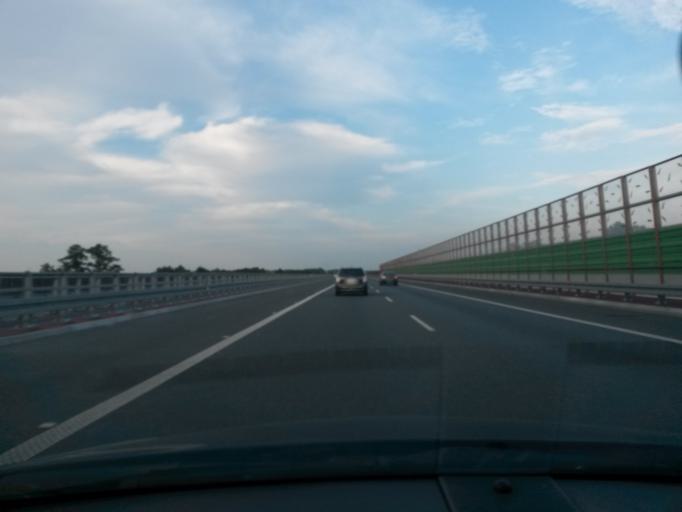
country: PL
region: Lodz Voivodeship
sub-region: Powiat skierniewicki
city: Bolimow
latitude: 52.0669
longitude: 20.1800
